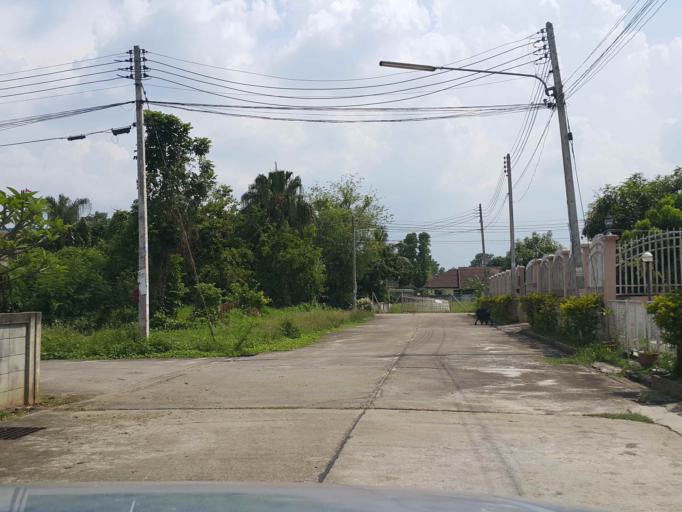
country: TH
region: Chiang Mai
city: Hang Dong
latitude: 18.7077
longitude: 98.9475
